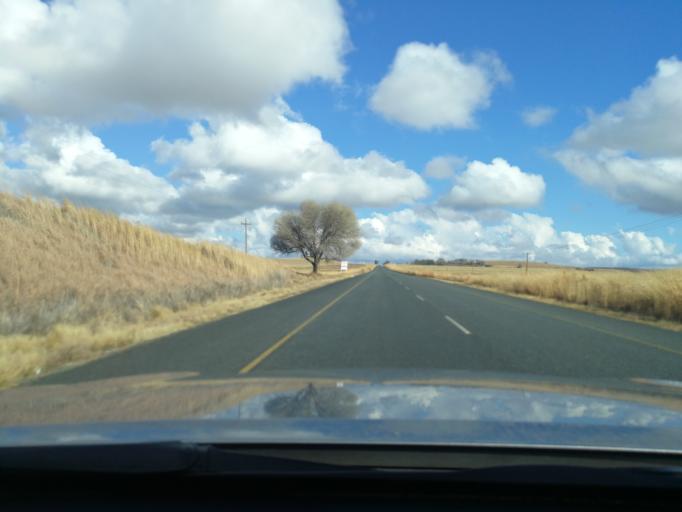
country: ZA
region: Orange Free State
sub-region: Thabo Mofutsanyana District Municipality
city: Reitz
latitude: -27.9868
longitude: 28.3745
